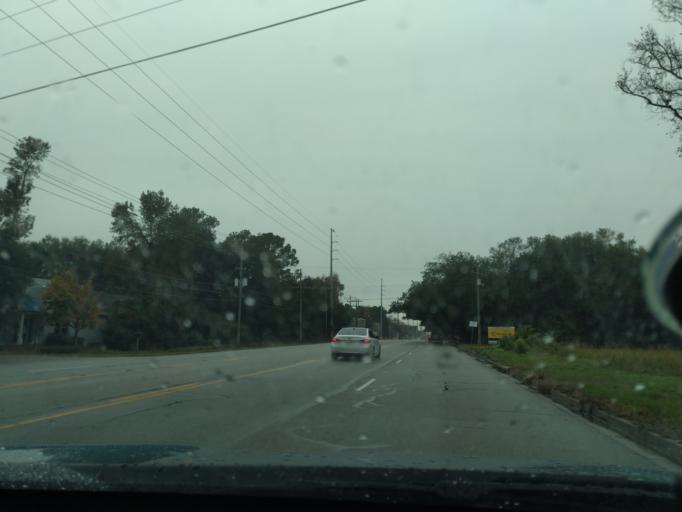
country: US
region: South Carolina
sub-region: Charleston County
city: Folly Beach
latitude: 32.7123
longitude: -79.9646
